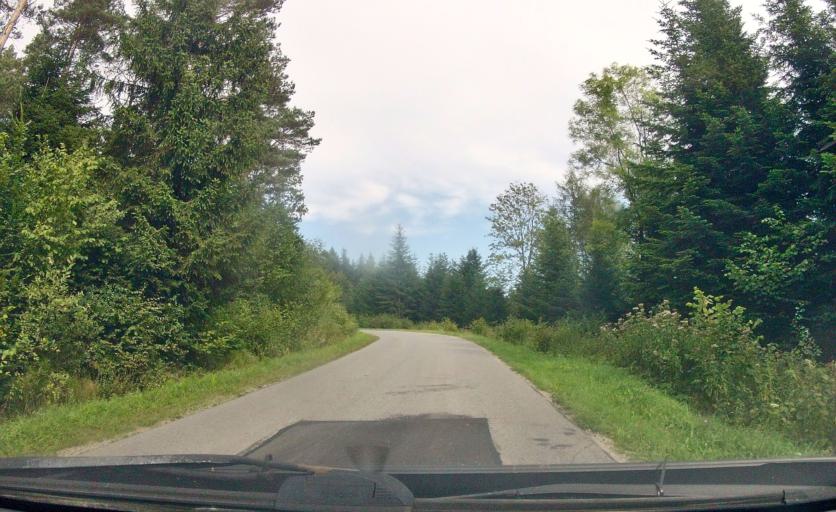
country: PL
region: Subcarpathian Voivodeship
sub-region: Powiat krosnienski
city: Dukla
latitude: 49.4999
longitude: 21.6026
